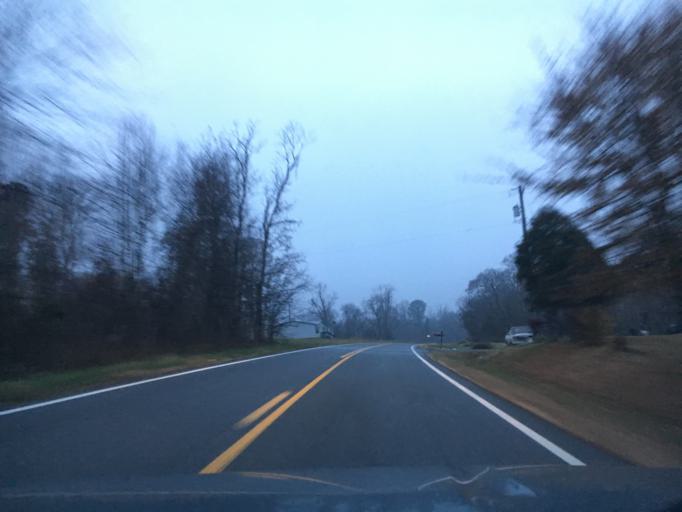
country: US
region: Virginia
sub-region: Halifax County
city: Mountain Road
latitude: 36.6841
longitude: -78.9937
